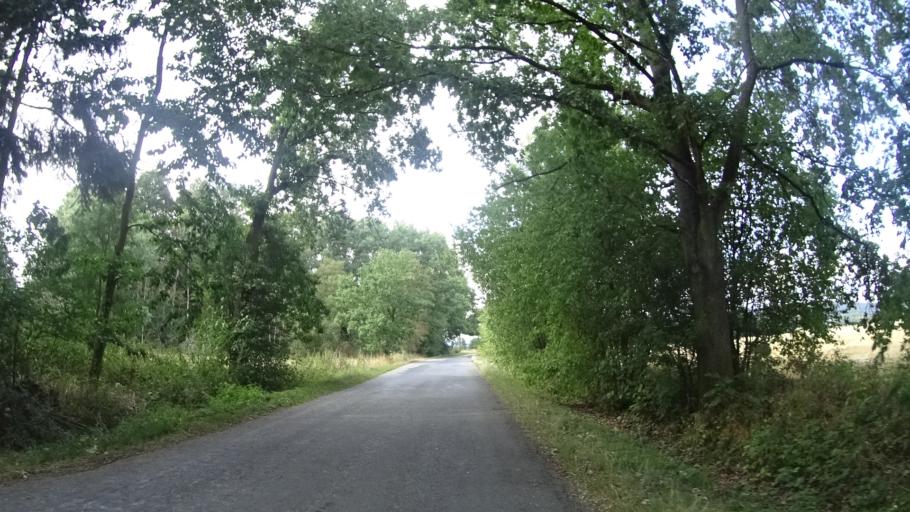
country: CZ
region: Olomoucky
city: Dubicko
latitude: 49.8067
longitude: 16.9416
